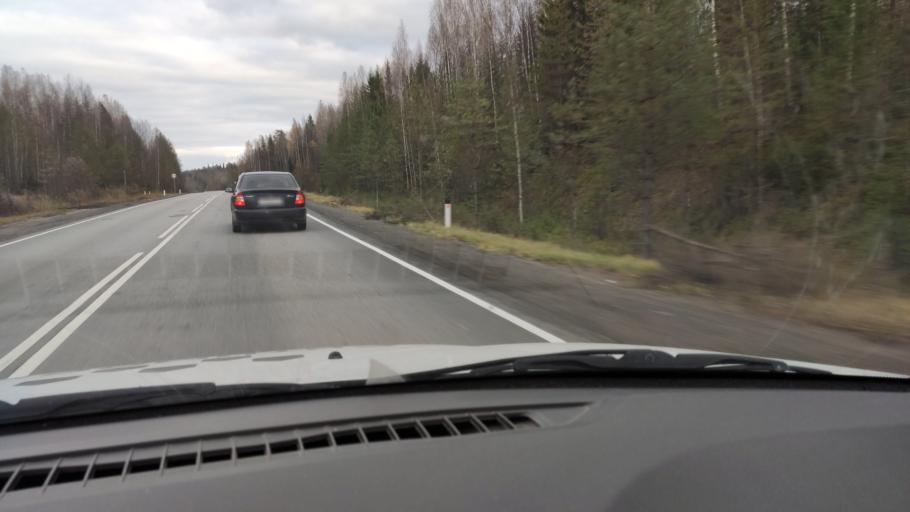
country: RU
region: Kirov
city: Chernaya Kholunitsa
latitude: 58.8661
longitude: 51.5731
